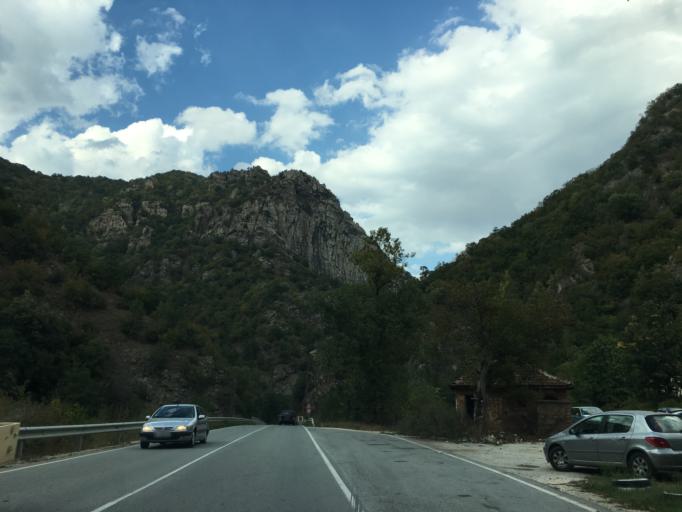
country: BG
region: Pazardzhik
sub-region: Obshtina Septemvri
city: Septemvri
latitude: 42.1070
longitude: 24.1059
